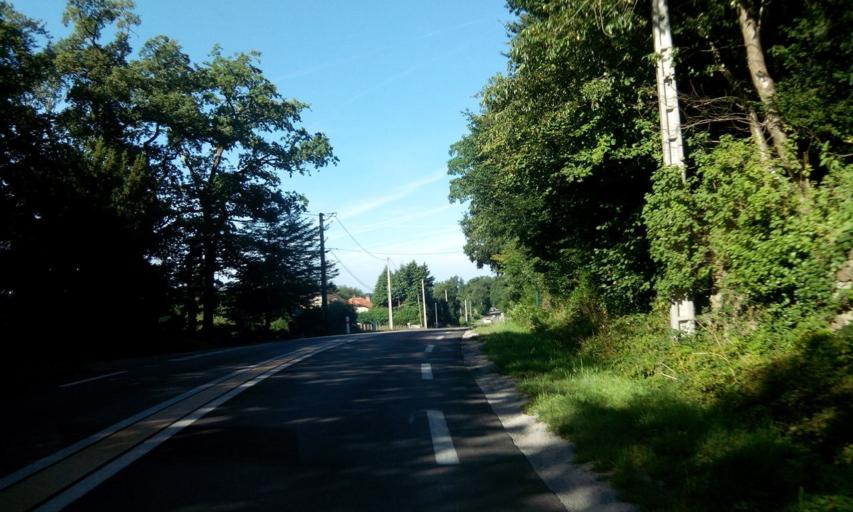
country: FR
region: Limousin
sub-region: Departement de la Haute-Vienne
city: Panazol
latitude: 45.8435
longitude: 1.3364
